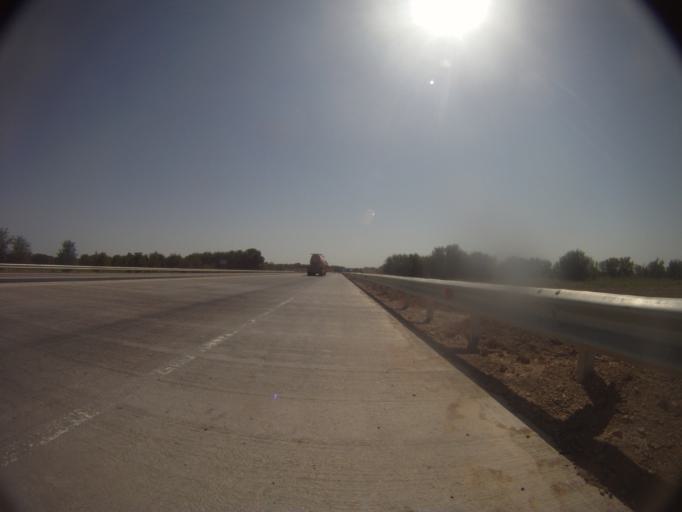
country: KZ
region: Ongtustik Qazaqstan
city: Turkestan
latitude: 43.1558
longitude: 68.5619
